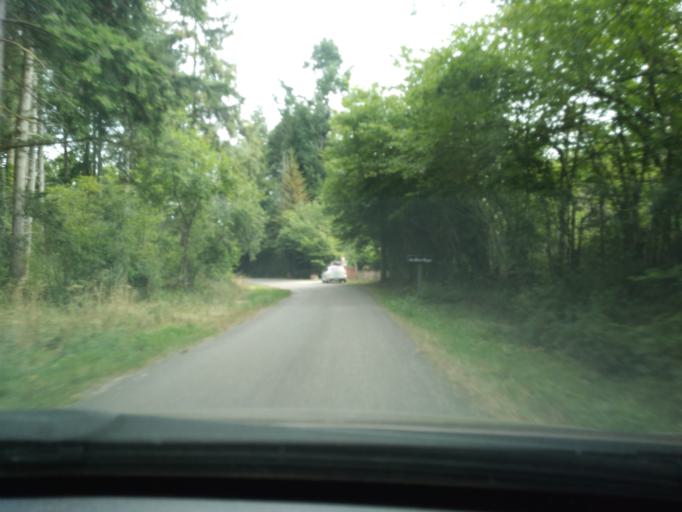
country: FR
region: Bourgogne
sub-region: Departement de la Cote-d'Or
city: Saulieu
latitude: 47.3472
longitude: 4.0924
